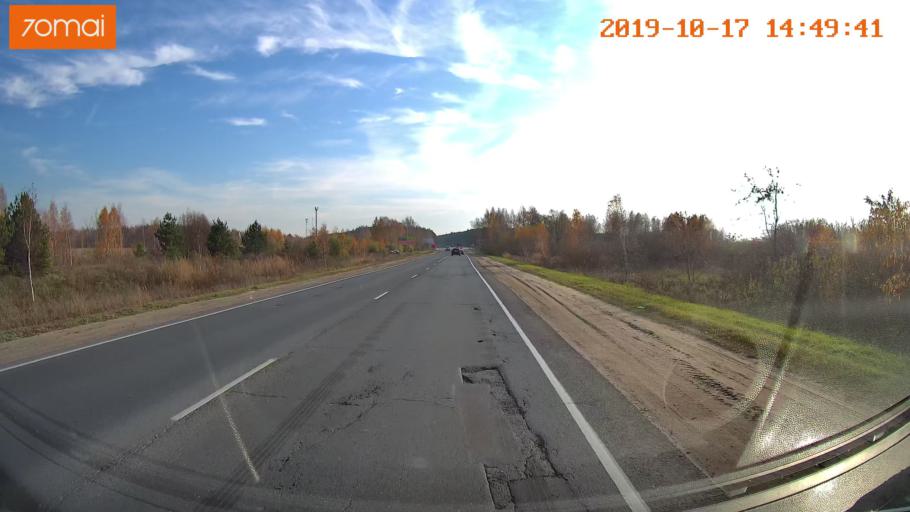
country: RU
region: Rjazan
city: Polyany
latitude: 54.7437
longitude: 39.8404
